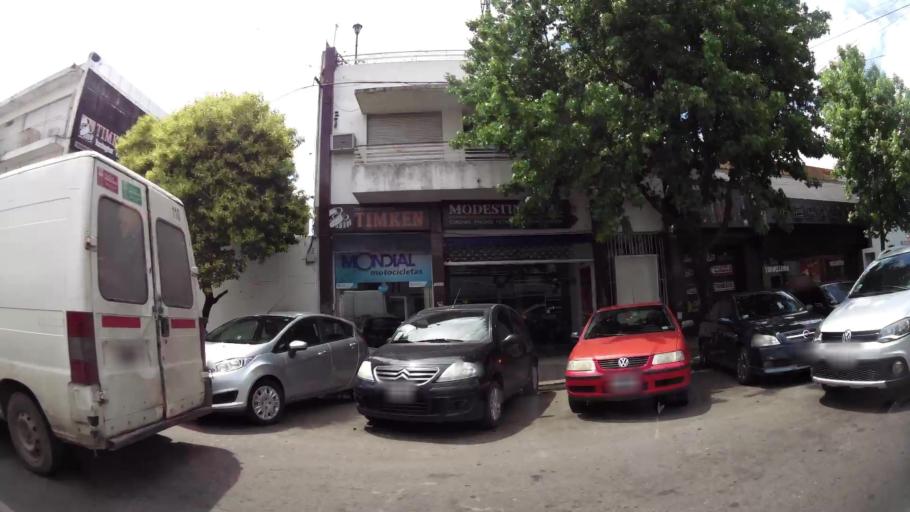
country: AR
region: Santa Fe
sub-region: Departamento de Rosario
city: Rosario
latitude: -32.9615
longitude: -60.6404
